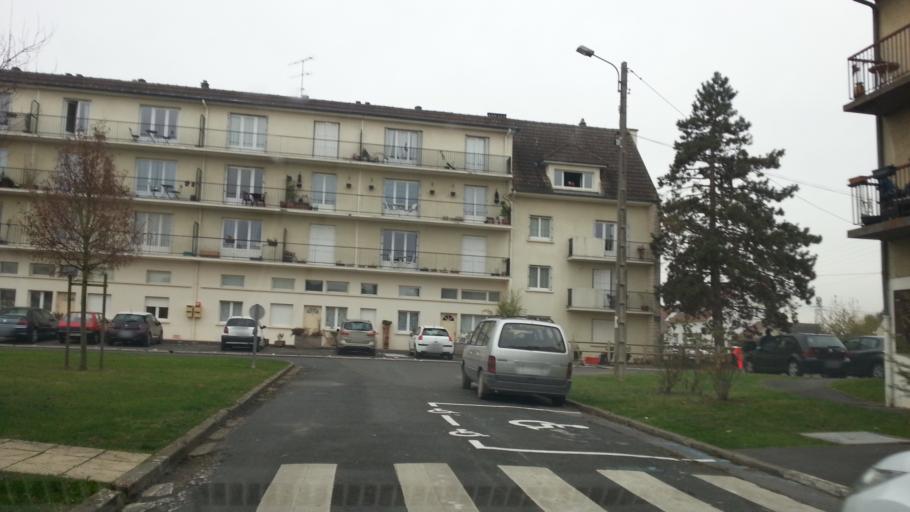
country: FR
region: Picardie
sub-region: Departement de l'Oise
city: Villers-sous-Saint-Leu
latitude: 49.2145
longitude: 2.3962
